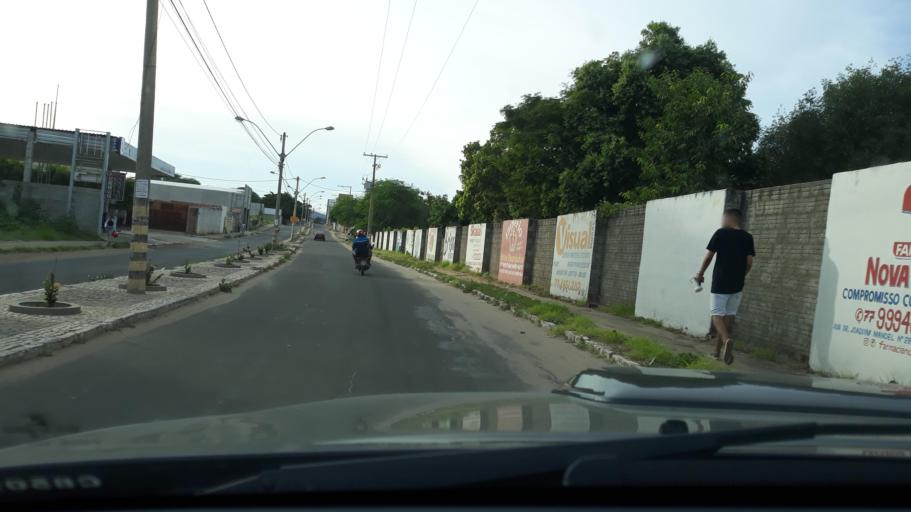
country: BR
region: Bahia
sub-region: Guanambi
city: Guanambi
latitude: -14.2344
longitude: -42.7738
